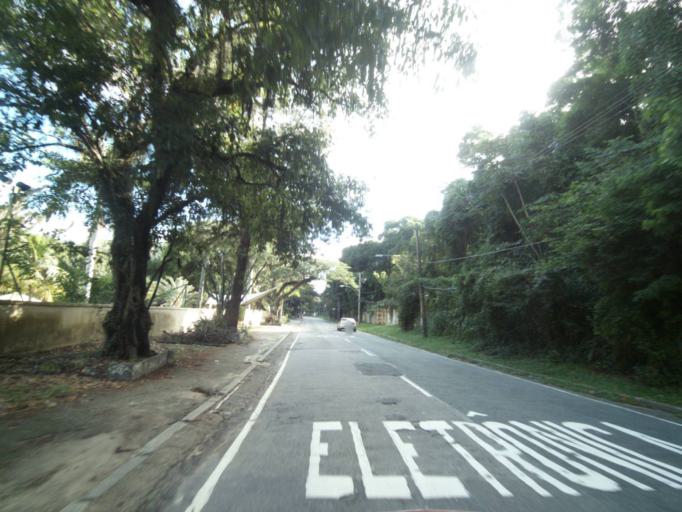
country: BR
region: Rio de Janeiro
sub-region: Rio De Janeiro
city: Rio de Janeiro
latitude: -22.9274
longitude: -43.3202
